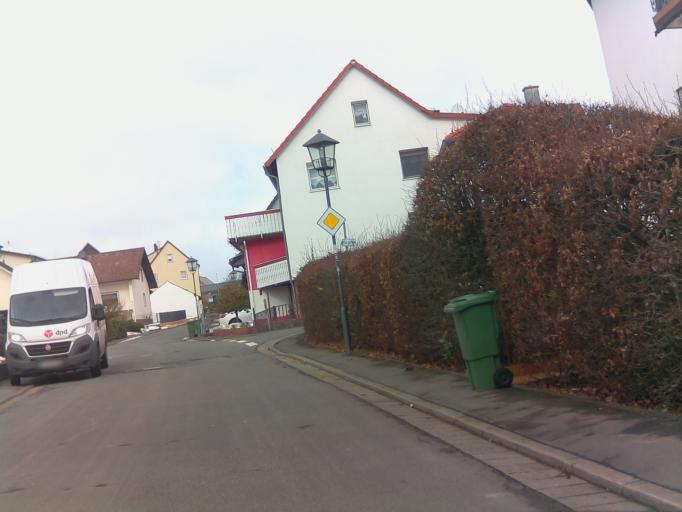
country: DE
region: Hesse
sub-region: Regierungsbezirk Darmstadt
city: Hesseneck
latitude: 49.6476
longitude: 9.0810
